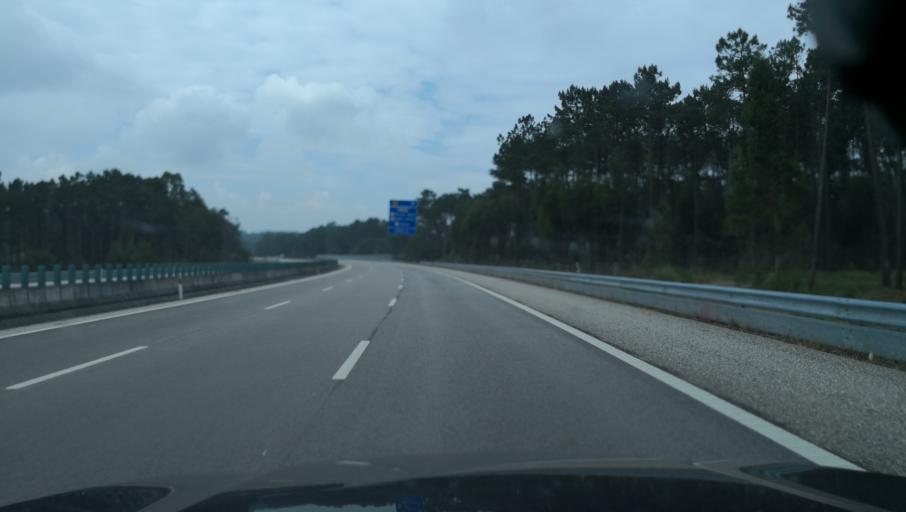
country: PT
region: Leiria
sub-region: Leiria
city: Monte Redondo
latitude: 39.8746
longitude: -8.8231
